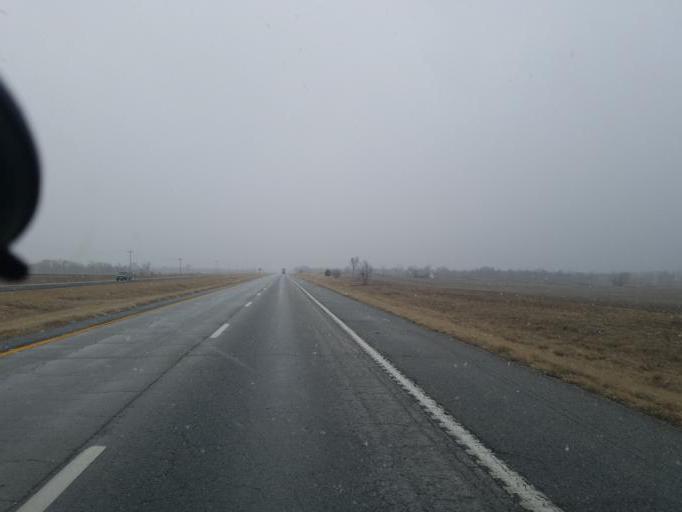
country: US
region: Missouri
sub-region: Macon County
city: La Plata
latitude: 39.9362
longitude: -92.4769
